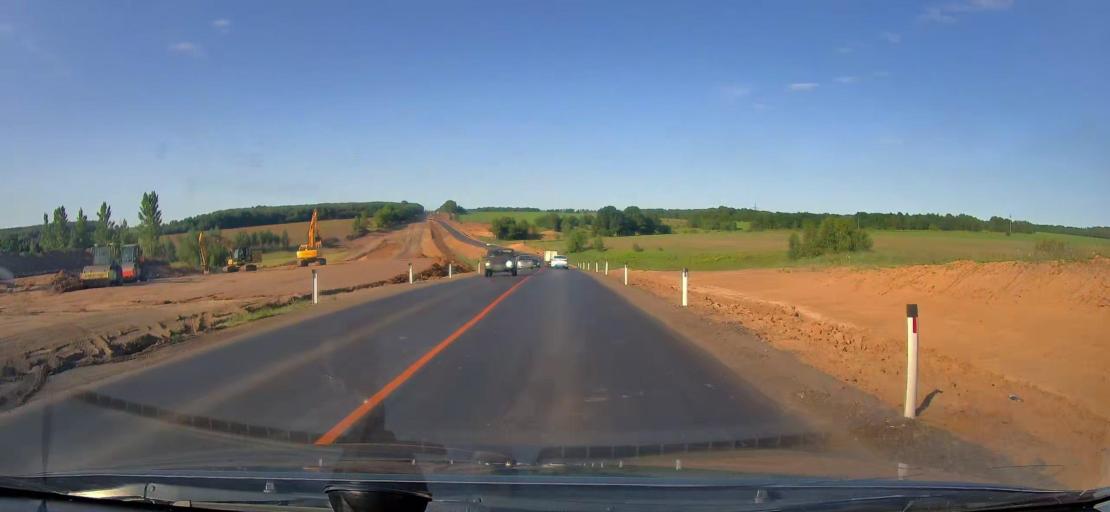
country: RU
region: Tula
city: Bol'shoye Skuratovo
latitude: 53.4165
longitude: 36.7824
